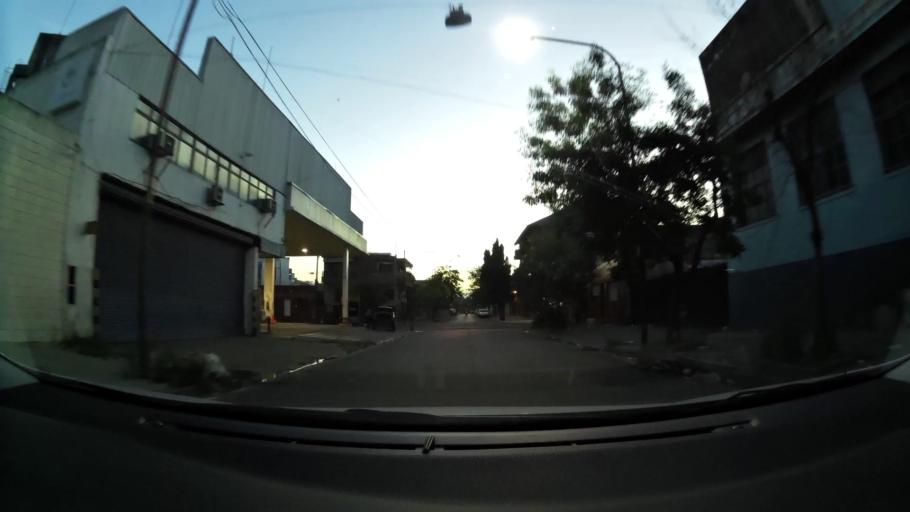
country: AR
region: Buenos Aires F.D.
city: Villa Lugano
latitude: -34.6958
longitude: -58.4691
